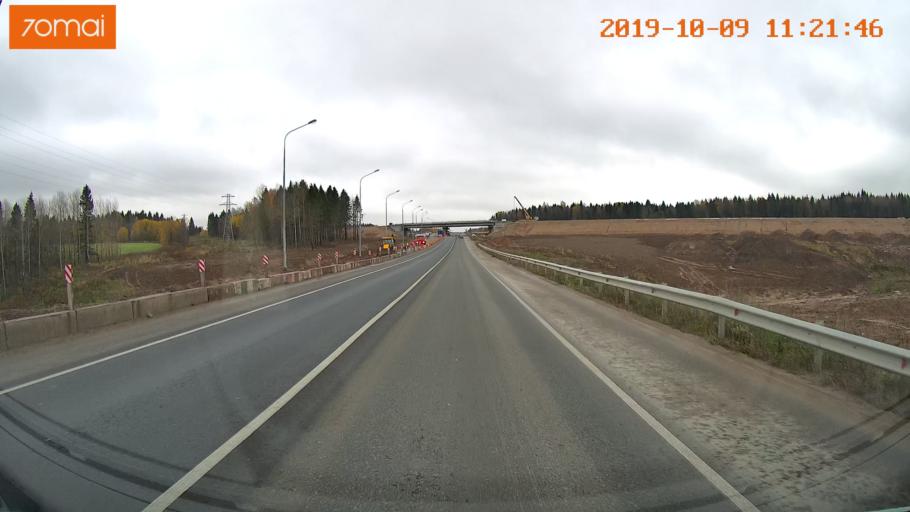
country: RU
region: Vologda
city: Vologda
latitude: 59.1369
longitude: 39.9523
